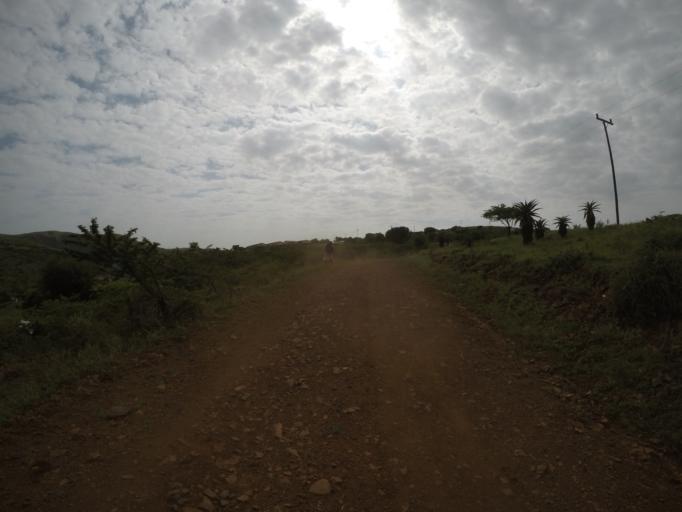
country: ZA
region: KwaZulu-Natal
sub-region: uThungulu District Municipality
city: Empangeni
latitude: -28.6247
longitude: 31.8979
